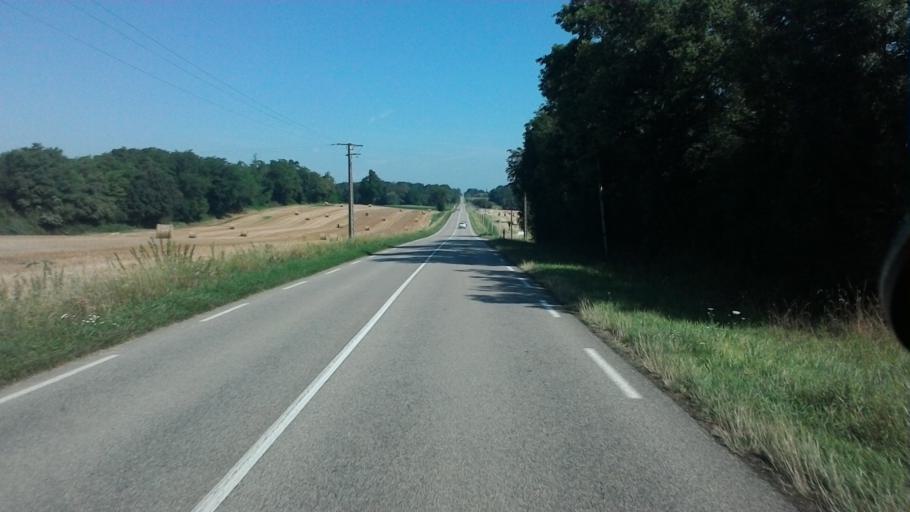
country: FR
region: Rhone-Alpes
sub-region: Departement de l'Ain
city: Saint-Trivier-de-Courtes
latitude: 46.4708
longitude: 5.0758
